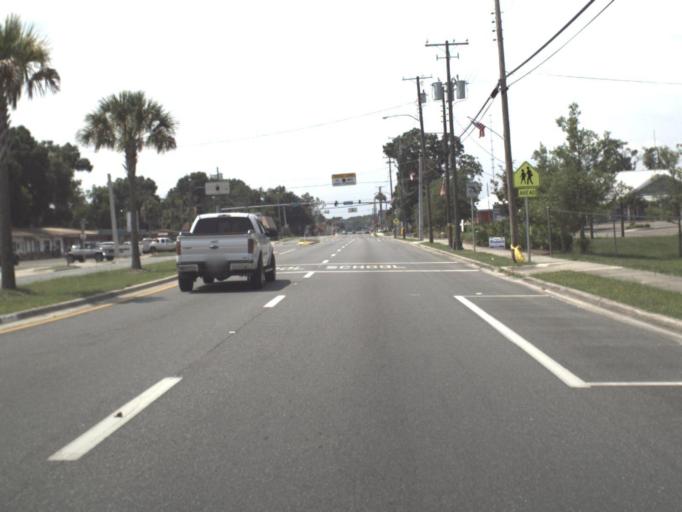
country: US
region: Florida
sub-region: Levy County
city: Chiefland
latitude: 29.4837
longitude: -82.8598
